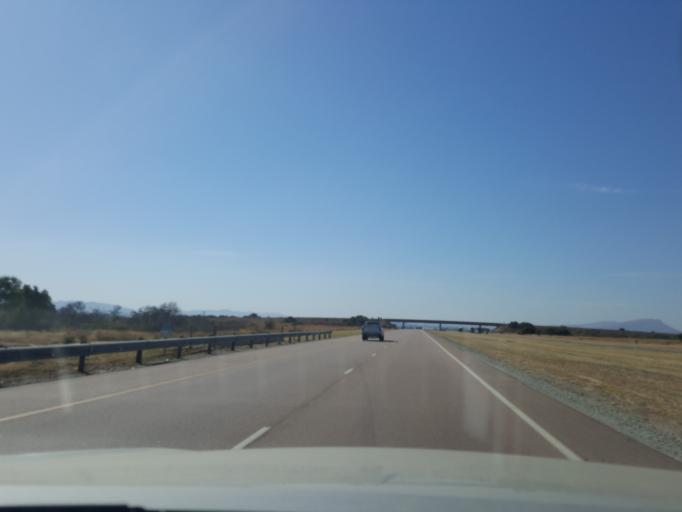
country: ZA
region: North-West
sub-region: Bojanala Platinum District Municipality
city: Brits
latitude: -25.6882
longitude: 27.7539
